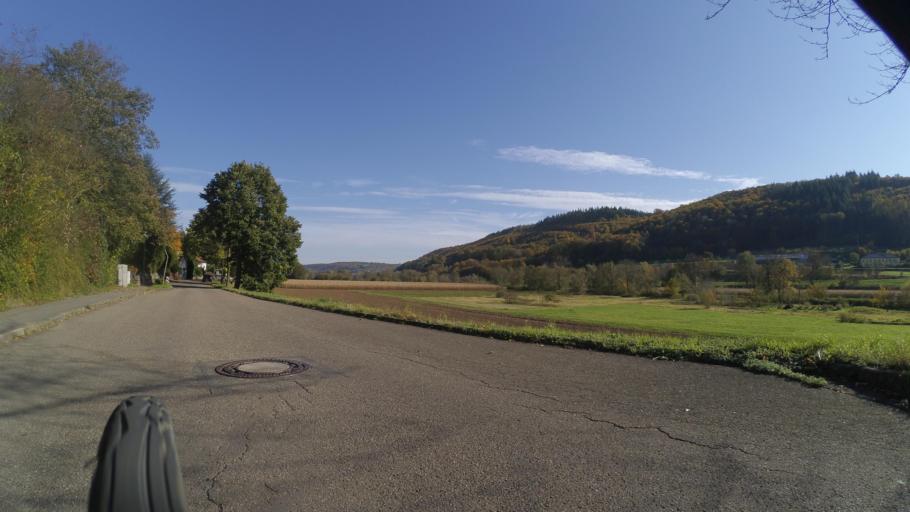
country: DE
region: Baden-Wuerttemberg
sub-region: Regierungsbezirk Stuttgart
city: Zweiflingen
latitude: 49.2941
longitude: 9.5225
